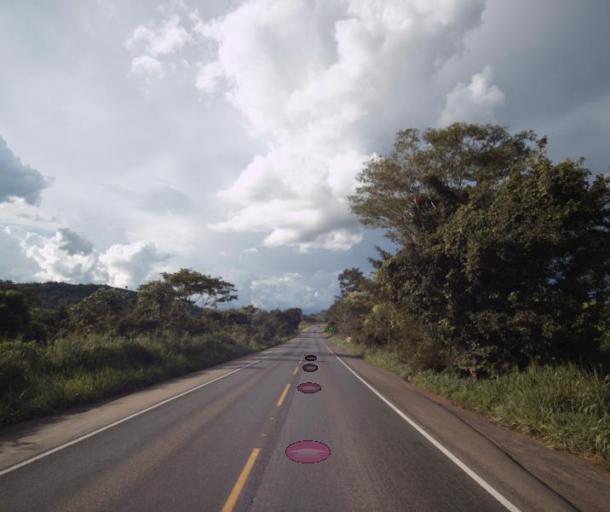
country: BR
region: Goias
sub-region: Rialma
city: Rialma
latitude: -15.2935
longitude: -49.5686
